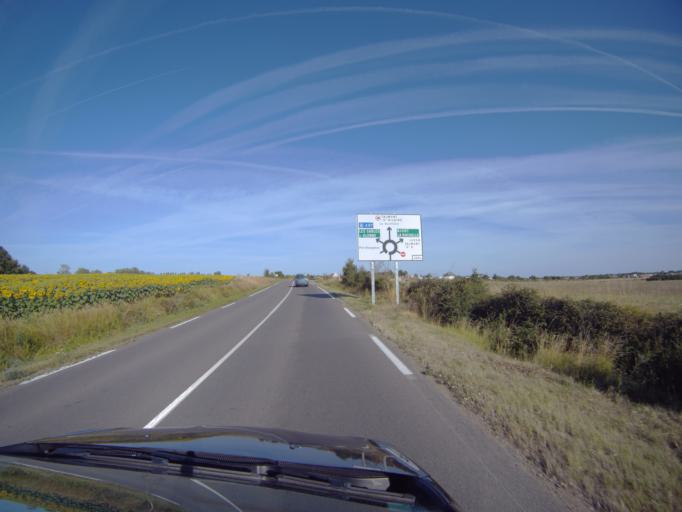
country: FR
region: Pays de la Loire
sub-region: Departement de la Vendee
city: Saint-Hilaire-de-Talmont
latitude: 46.4569
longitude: -1.6054
